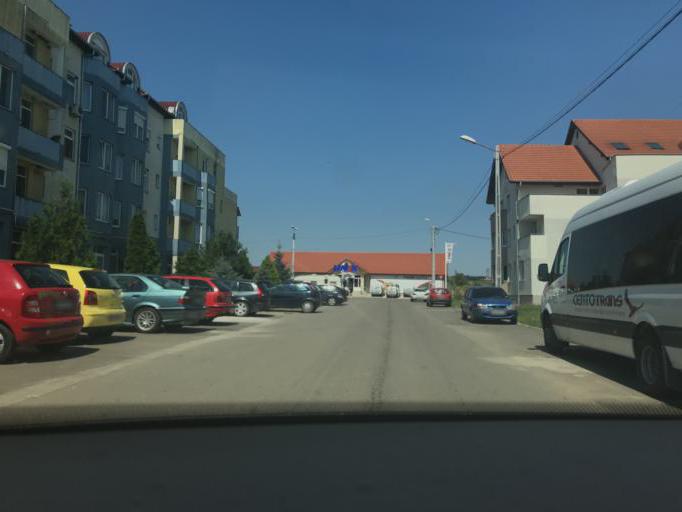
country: RO
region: Bihor
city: Margita
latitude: 47.3553
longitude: 22.3478
